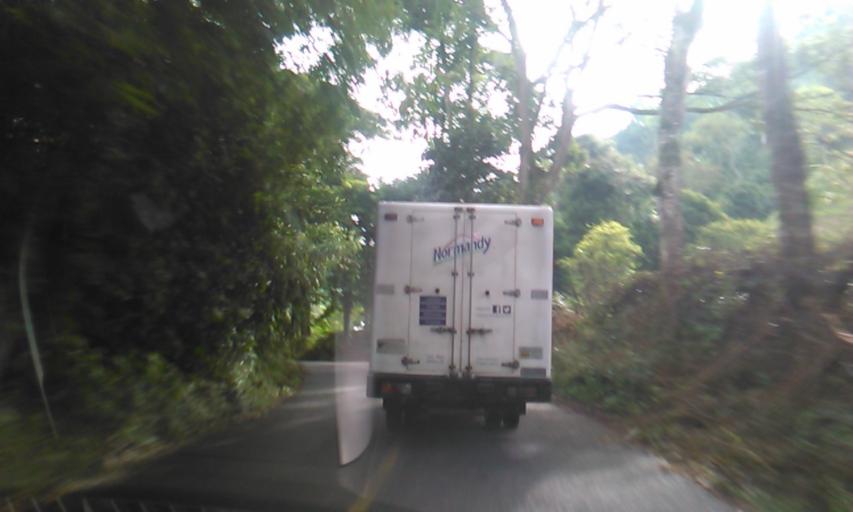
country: CO
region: Quindio
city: Cordoba
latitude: 4.4115
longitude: -75.7014
